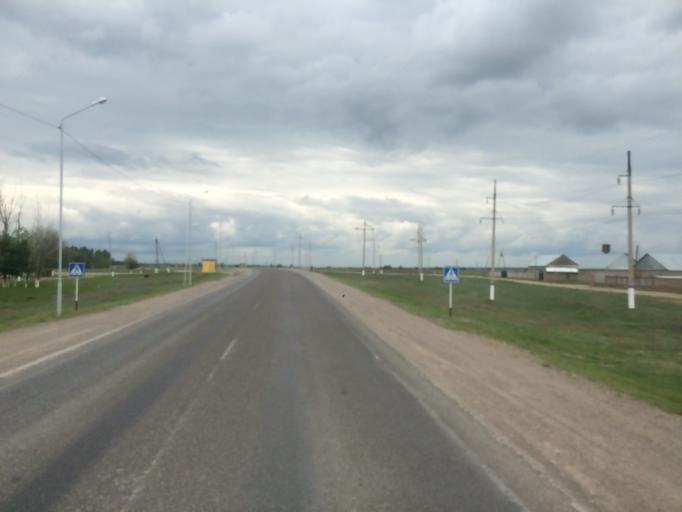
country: KG
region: Chuy
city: Sokuluk
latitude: 43.2471
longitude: 74.2980
